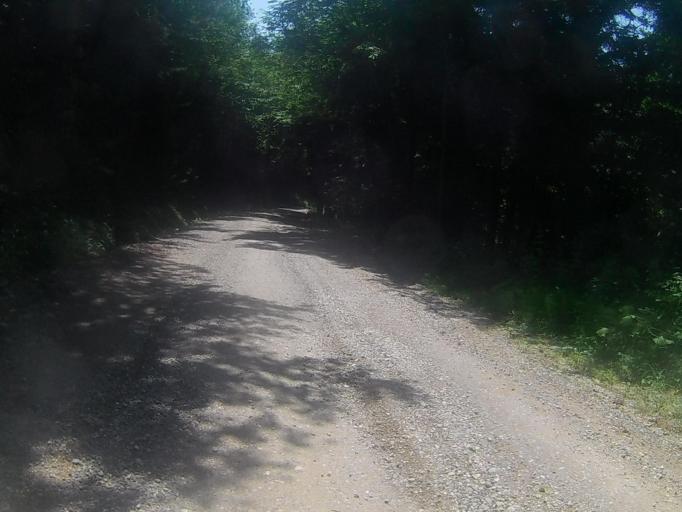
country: SI
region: Ruse
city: Bistrica ob Dravi
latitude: 46.5849
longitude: 15.5381
